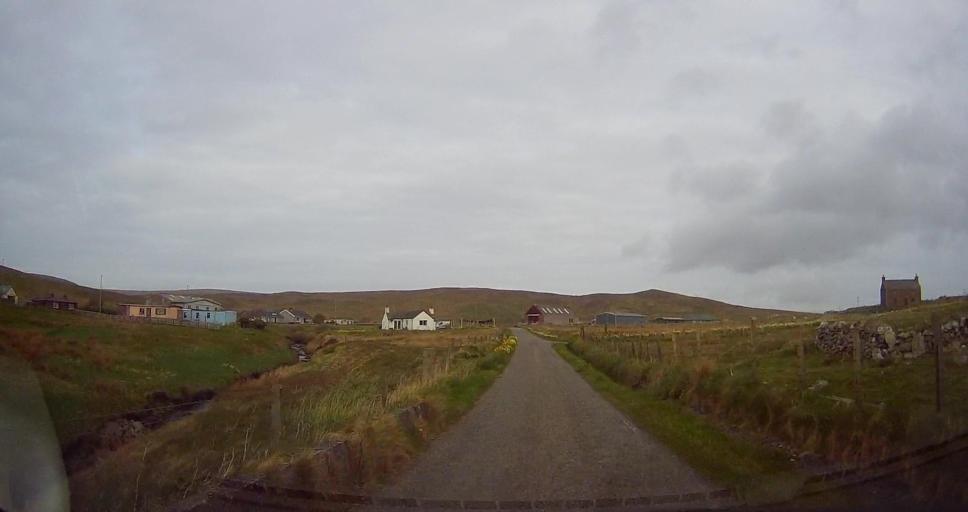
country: GB
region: Scotland
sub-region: Shetland Islands
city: Sandwick
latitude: 60.0540
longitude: -1.2237
